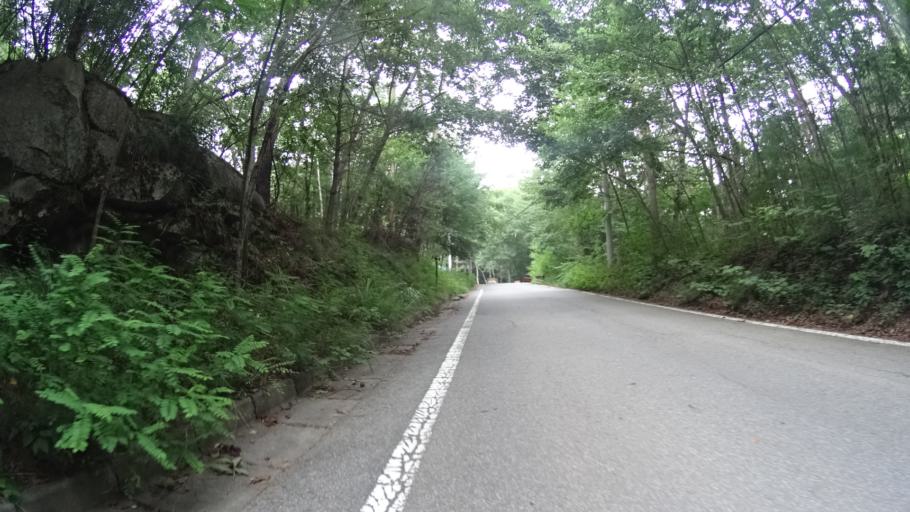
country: JP
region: Yamanashi
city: Nirasaki
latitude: 35.8919
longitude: 138.5640
